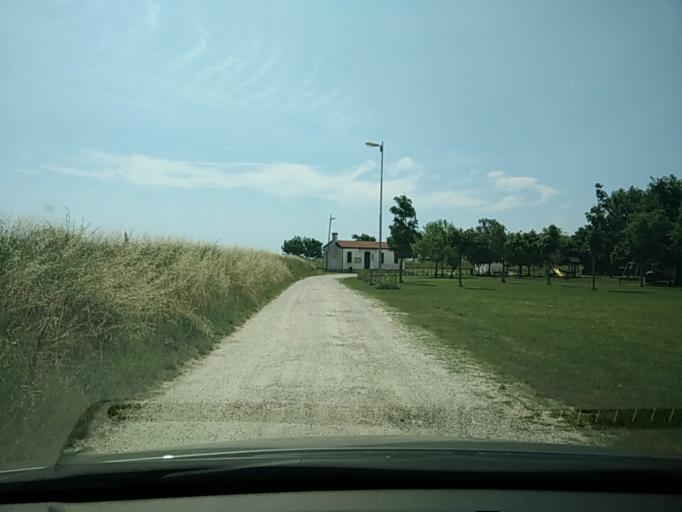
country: IT
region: Veneto
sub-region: Provincia di Venezia
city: Tessera
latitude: 45.4990
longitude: 12.3321
